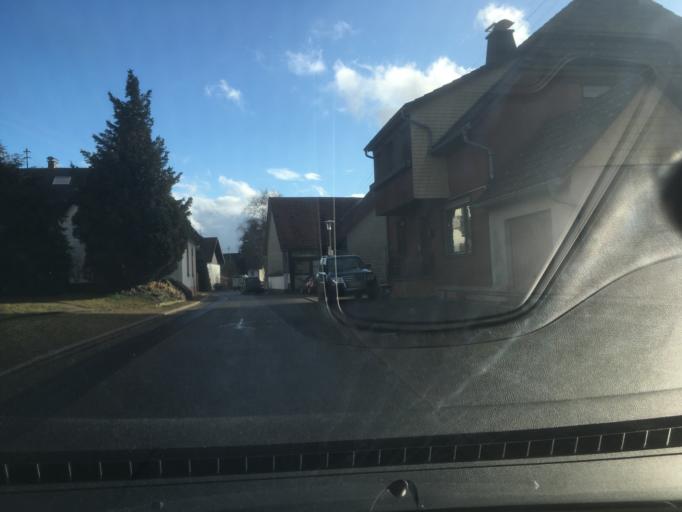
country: DE
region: Baden-Wuerttemberg
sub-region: Freiburg Region
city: Hochenschwand
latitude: 47.6917
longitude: 8.1443
